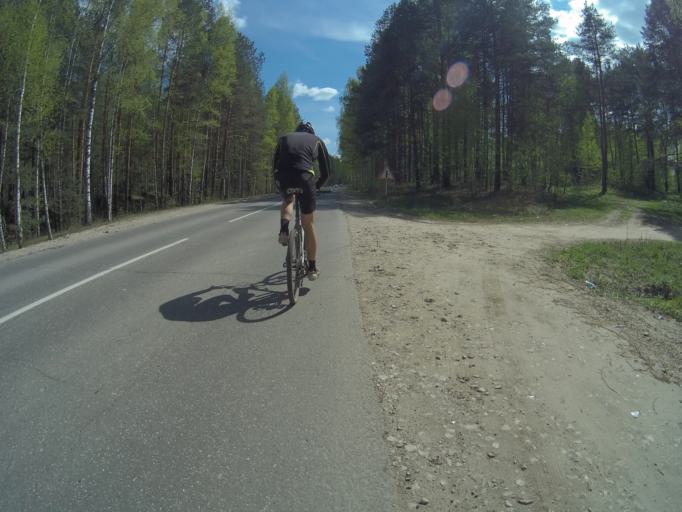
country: RU
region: Vladimir
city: Raduzhnyy
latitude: 55.9971
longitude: 40.2703
